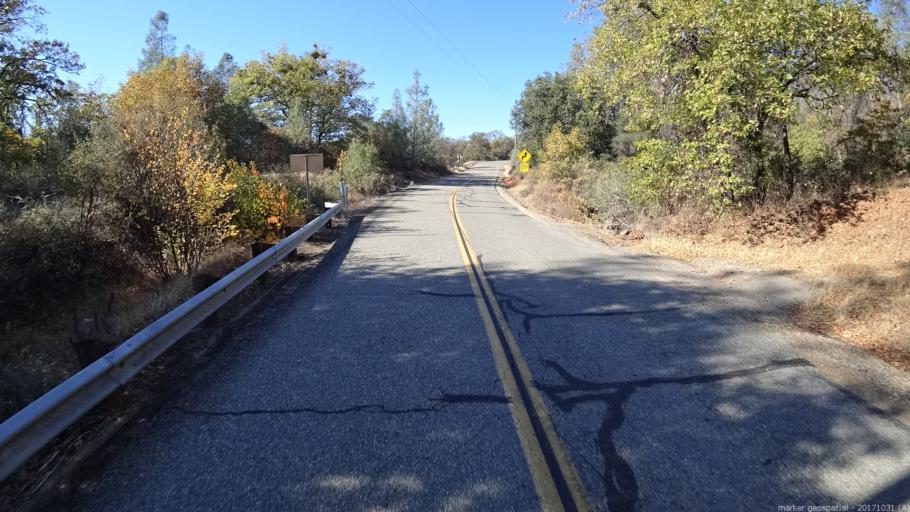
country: US
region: California
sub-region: Shasta County
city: Shingletown
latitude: 40.4913
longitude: -121.9993
